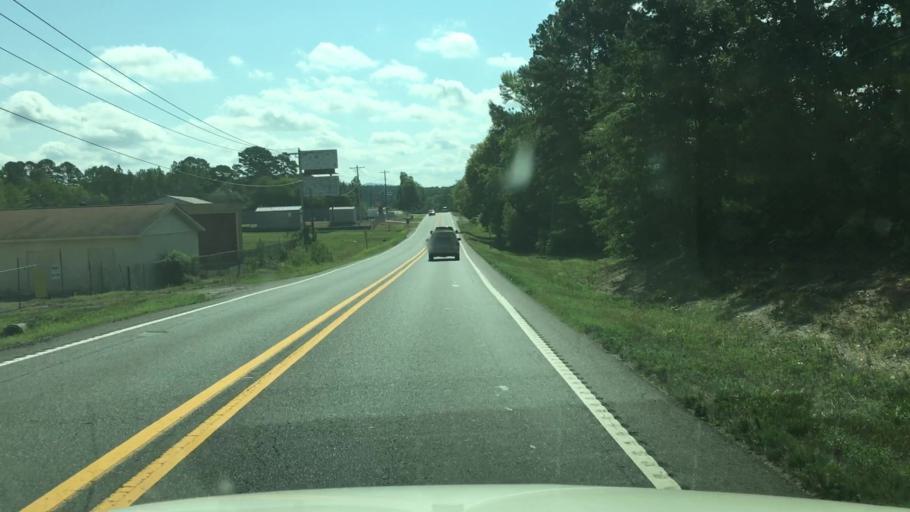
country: US
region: Arkansas
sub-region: Garland County
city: Piney
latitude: 34.5105
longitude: -93.2039
